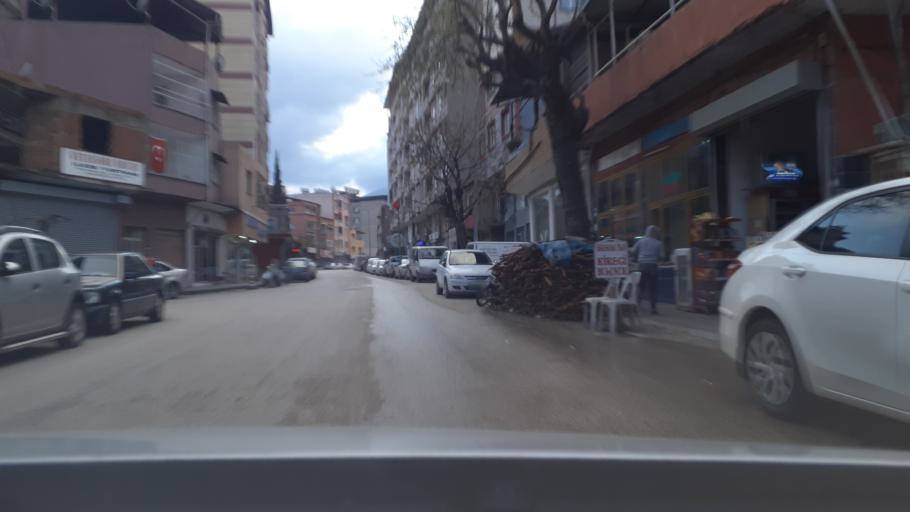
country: TR
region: Hatay
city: Kirikhan
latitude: 36.4968
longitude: 36.3597
